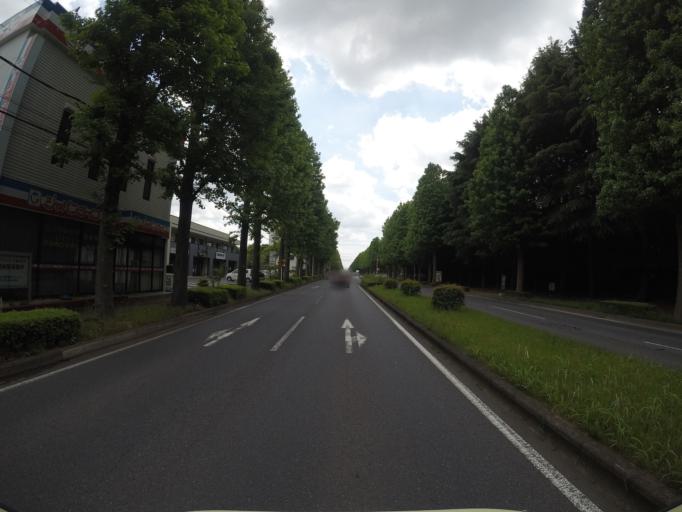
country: JP
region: Ibaraki
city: Naka
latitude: 36.0243
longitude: 140.1187
